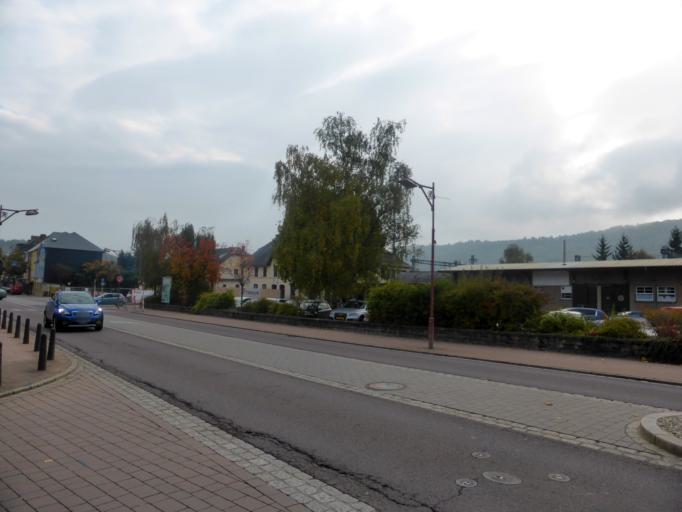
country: LU
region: Grevenmacher
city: Wasserbillig
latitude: 49.7130
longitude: 6.4972
